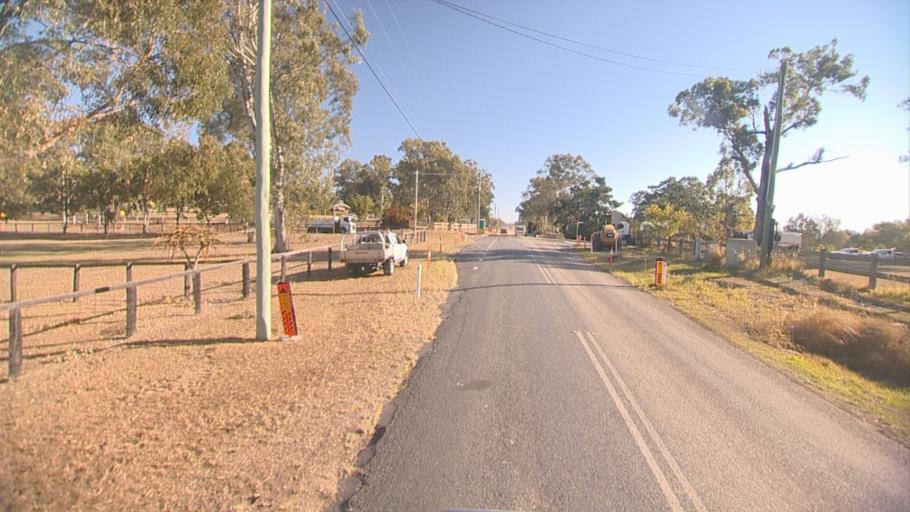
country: AU
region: Queensland
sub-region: Logan
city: Cedar Vale
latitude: -27.8317
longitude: 153.0057
